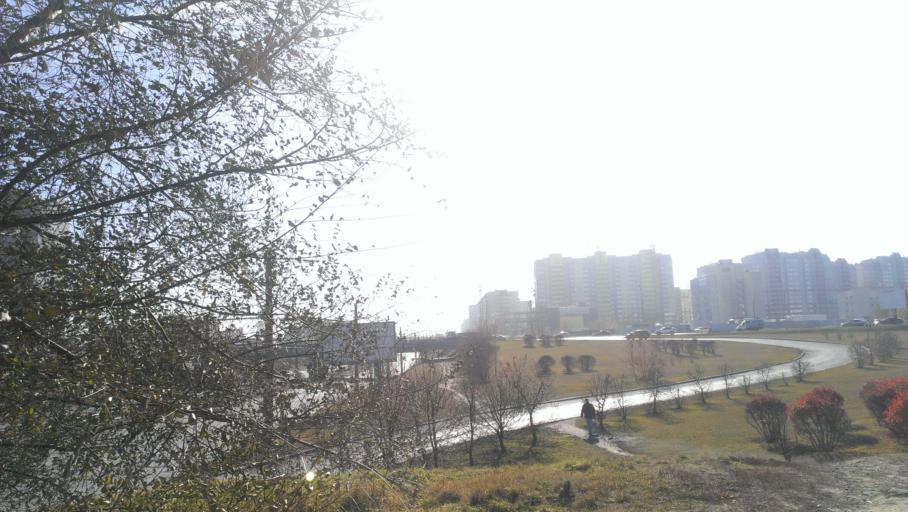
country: RU
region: Altai Krai
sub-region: Gorod Barnaulskiy
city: Barnaul
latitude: 53.3427
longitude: 83.6950
